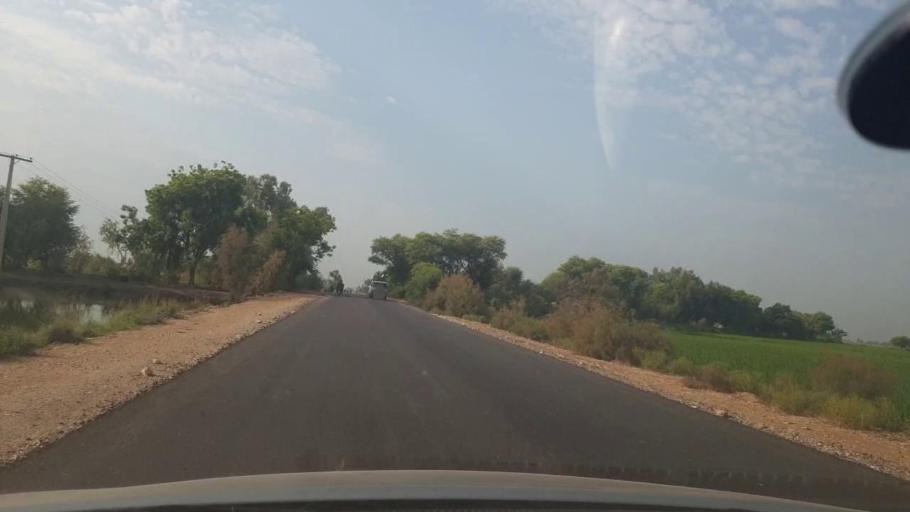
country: PK
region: Sindh
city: Jacobabad
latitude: 28.1116
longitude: 68.3266
